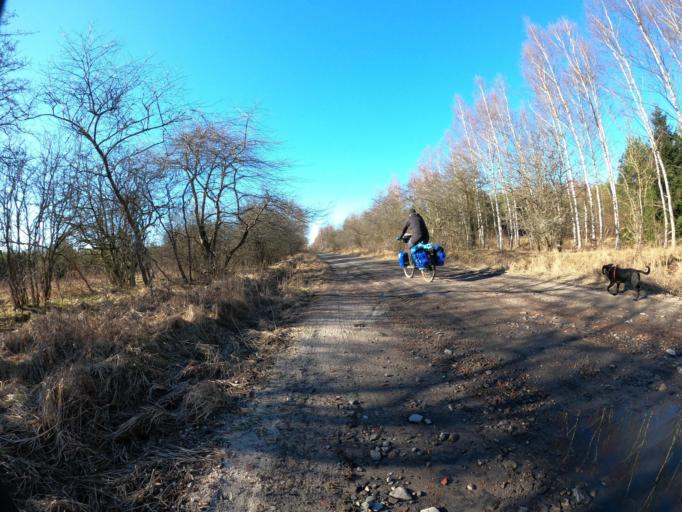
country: PL
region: West Pomeranian Voivodeship
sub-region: Powiat szczecinecki
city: Borne Sulinowo
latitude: 53.5478
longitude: 16.5587
